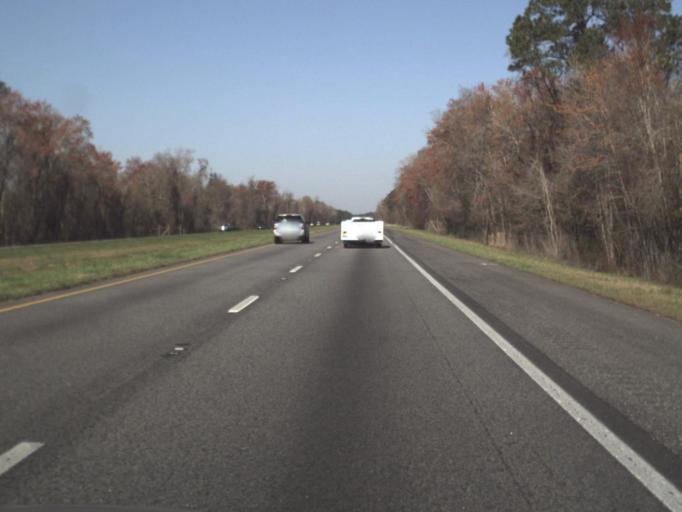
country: US
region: Florida
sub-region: Jefferson County
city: Monticello
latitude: 30.4649
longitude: -83.7950
